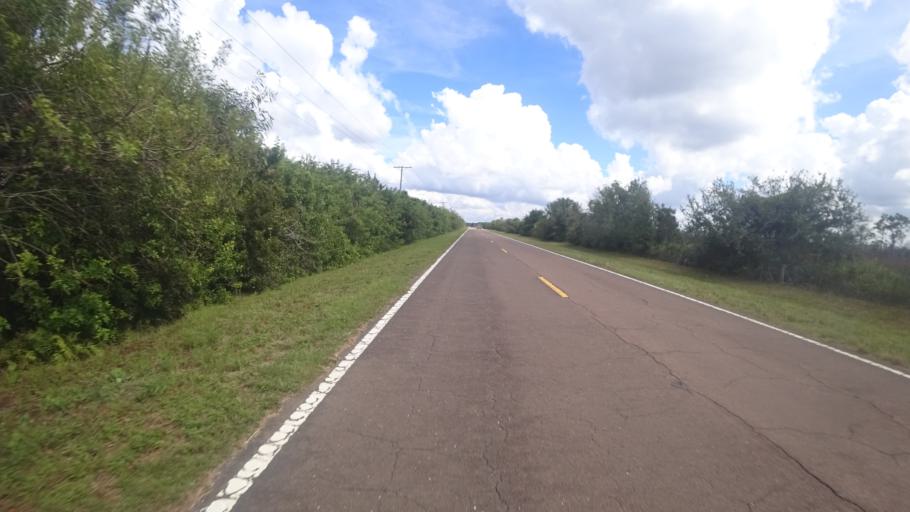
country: US
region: Florida
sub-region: Hillsborough County
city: Ruskin
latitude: 27.6540
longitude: -82.4600
